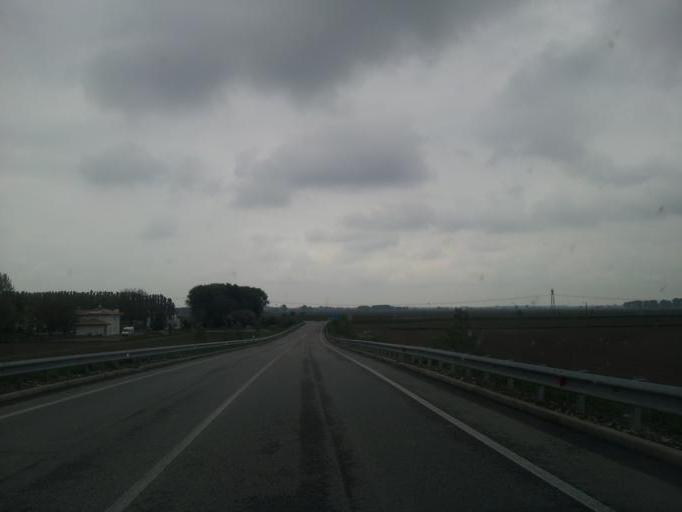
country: IT
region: Friuli Venezia Giulia
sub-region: Provincia di Udine
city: Ronchis
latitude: 45.8170
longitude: 13.0080
